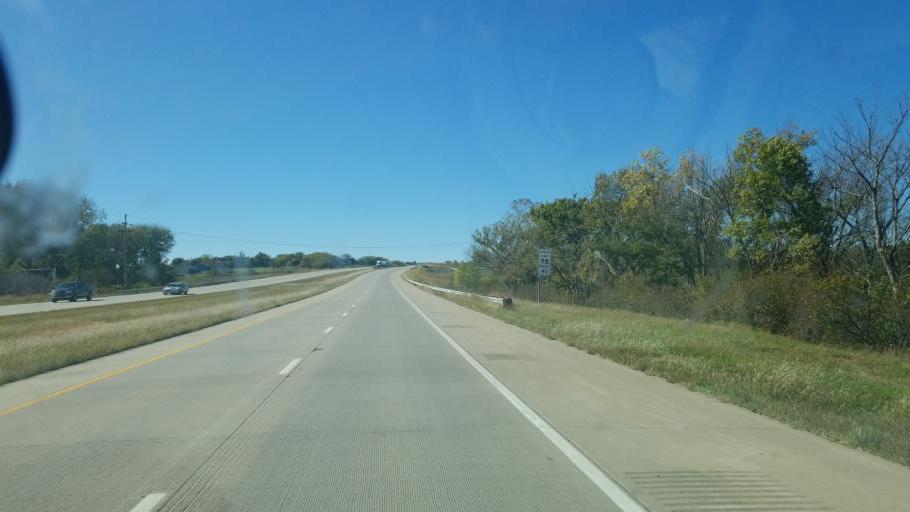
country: US
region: Kansas
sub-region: Wabaunsee County
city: Alma
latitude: 39.0584
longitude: -96.1636
